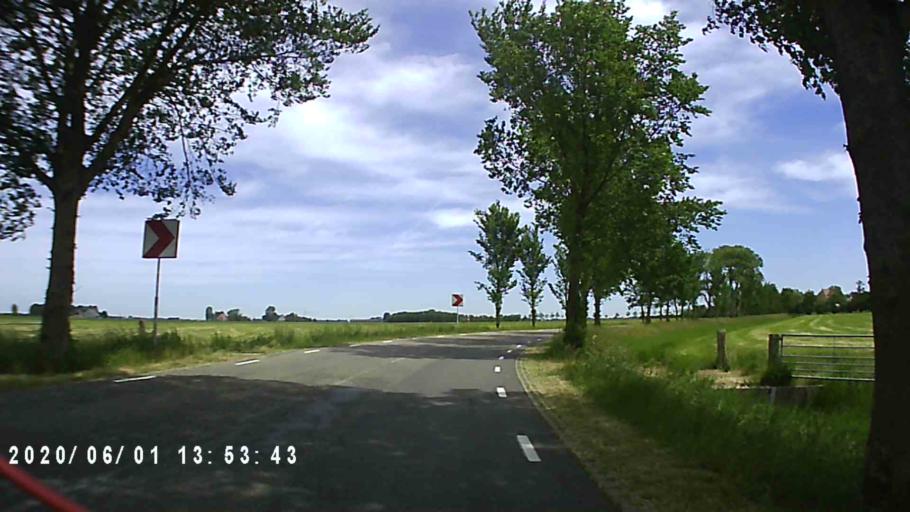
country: NL
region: Friesland
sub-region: Gemeente Littenseradiel
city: Wommels
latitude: 53.1044
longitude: 5.6324
